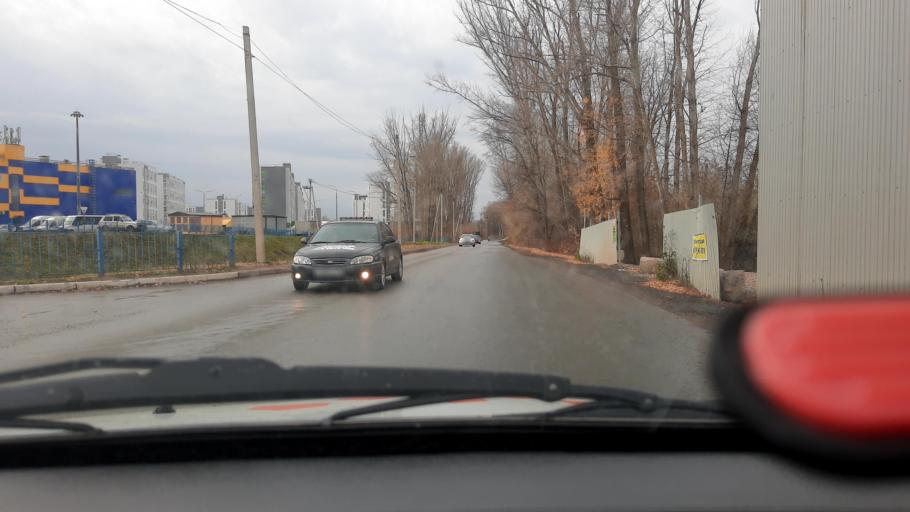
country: RU
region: Bashkortostan
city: Ufa
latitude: 54.6978
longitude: 55.9701
